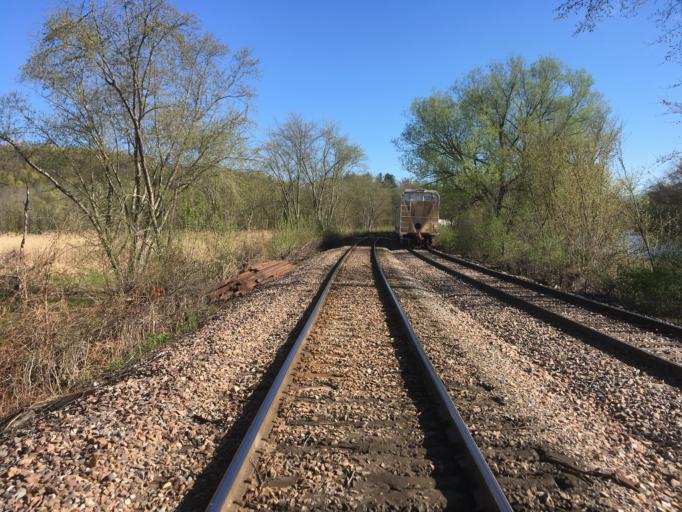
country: US
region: Vermont
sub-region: Rutland County
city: West Rutland
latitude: 43.6499
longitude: -73.0372
